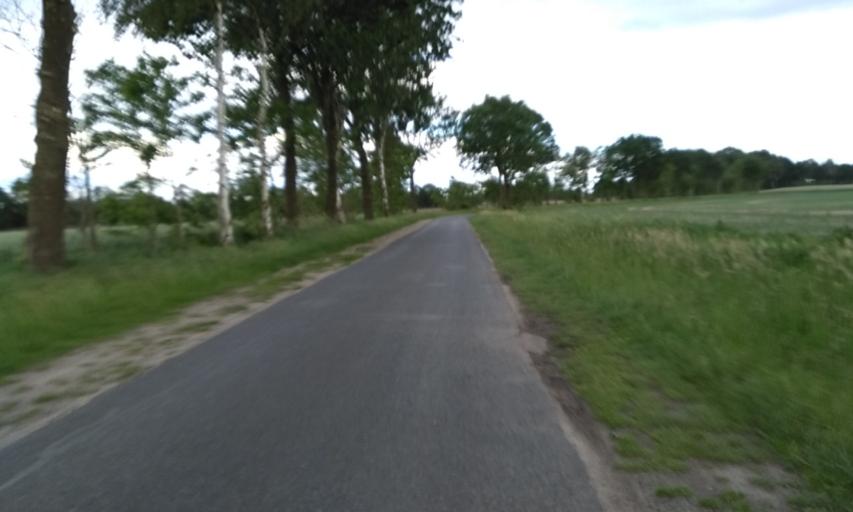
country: DE
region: Lower Saxony
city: Regesbostel
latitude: 53.3900
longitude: 9.6435
